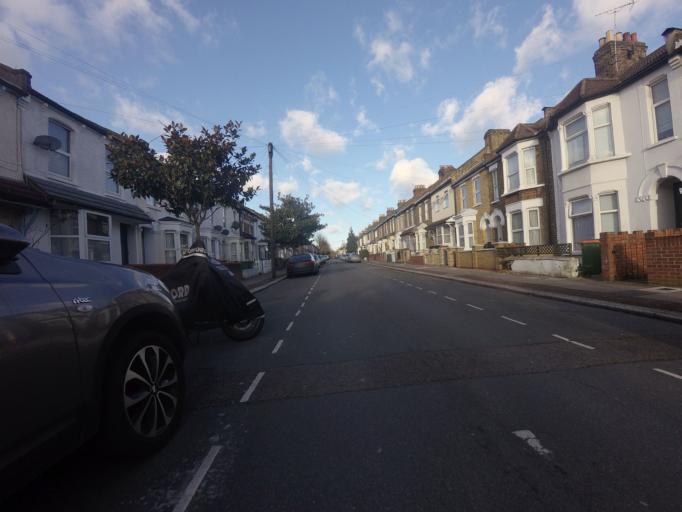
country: GB
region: England
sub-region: Greater London
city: East Ham
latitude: 51.5348
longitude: 0.0150
